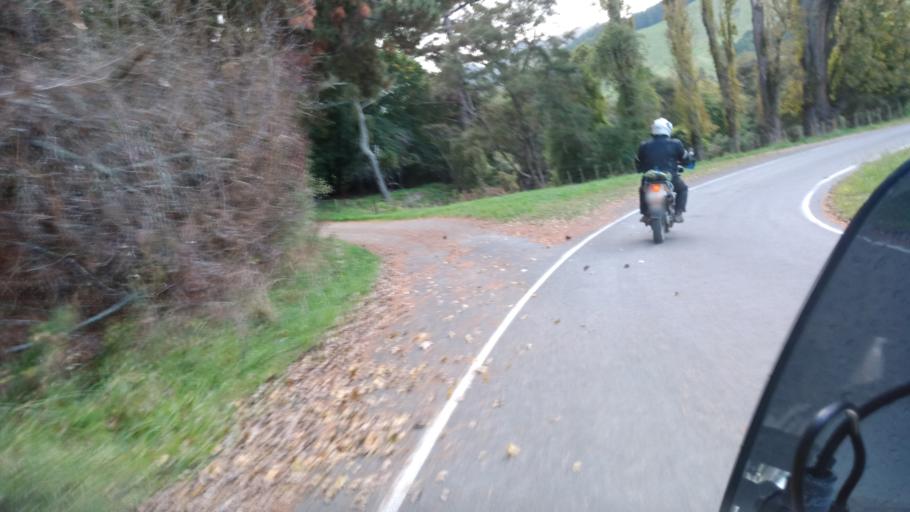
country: NZ
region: Gisborne
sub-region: Gisborne District
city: Gisborne
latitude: -38.4590
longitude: 177.6413
